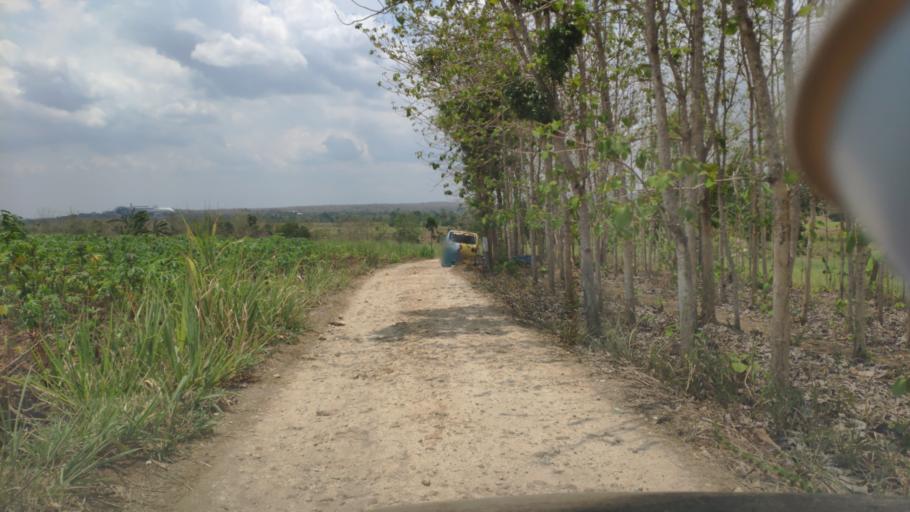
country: ID
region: Central Java
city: Ngapus
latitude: -6.9687
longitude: 111.2183
